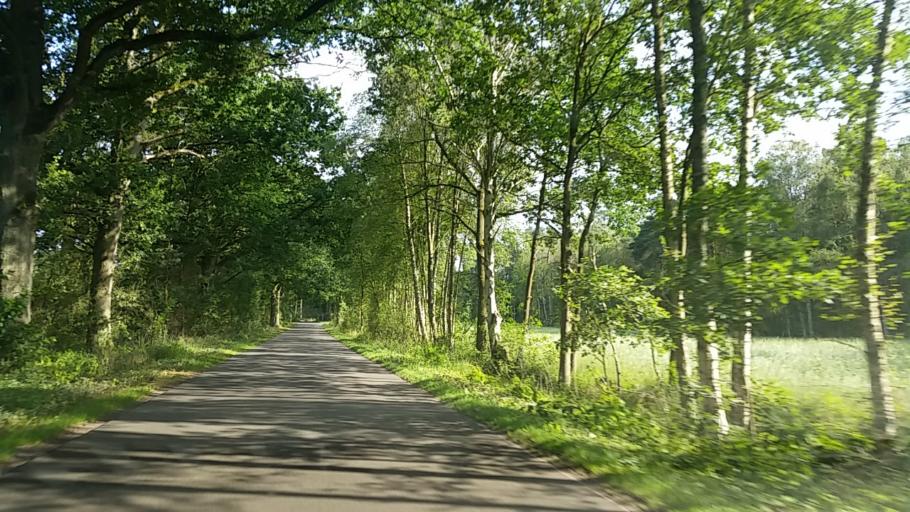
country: DE
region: Lower Saxony
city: Radbruch
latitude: 53.3197
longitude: 10.2454
